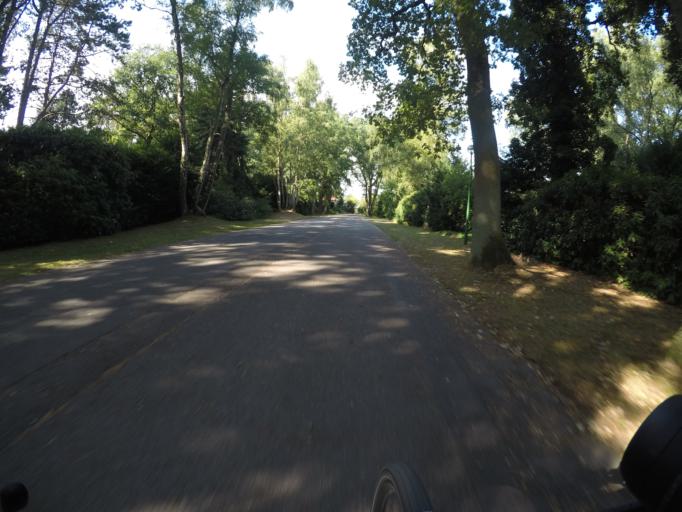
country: DE
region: Hamburg
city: Wandsbek
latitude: 53.5598
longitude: 10.1307
